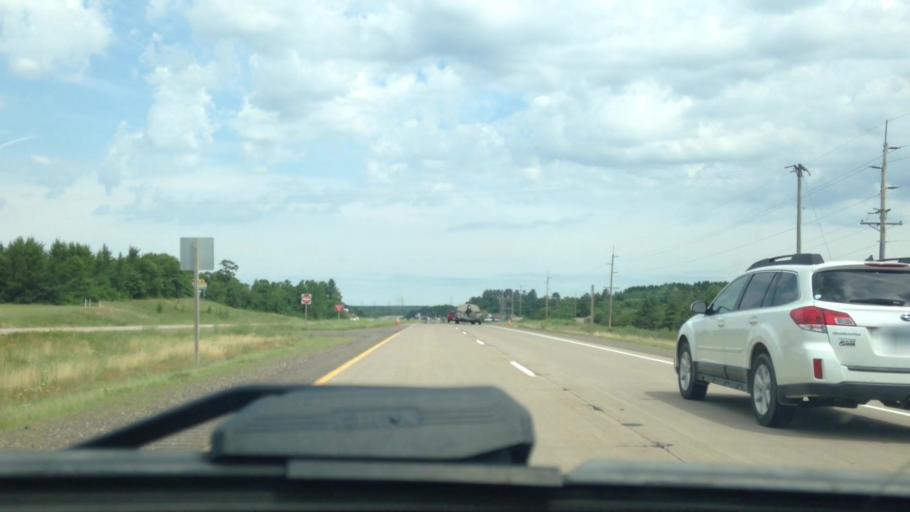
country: US
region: Wisconsin
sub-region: Douglas County
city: Lake Nebagamon
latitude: 46.2332
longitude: -91.8003
